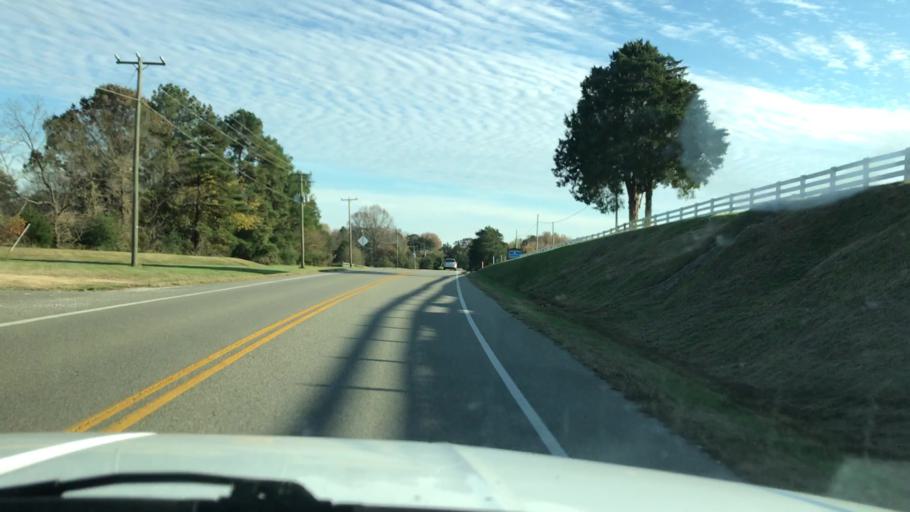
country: US
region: Virginia
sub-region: Goochland County
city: Goochland
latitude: 37.6448
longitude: -77.8177
